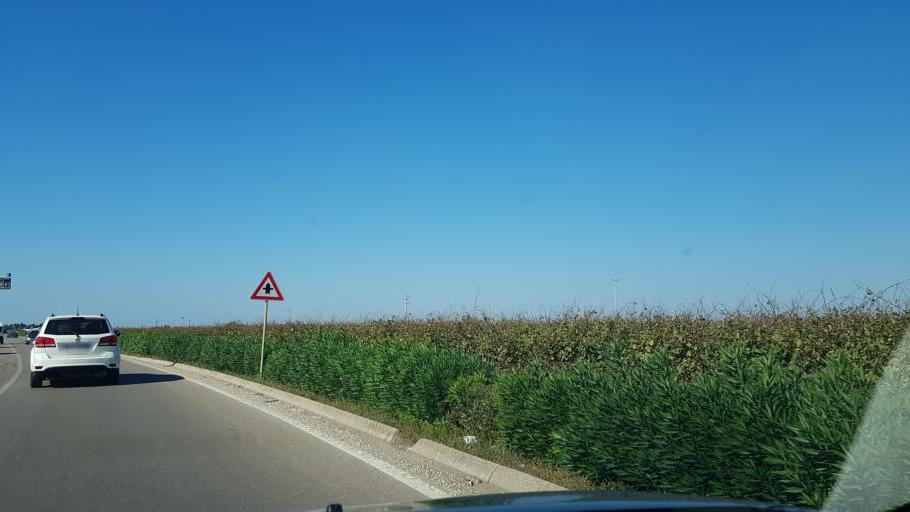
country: IT
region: Apulia
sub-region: Provincia di Lecce
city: Leverano
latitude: 40.2887
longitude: 17.9806
